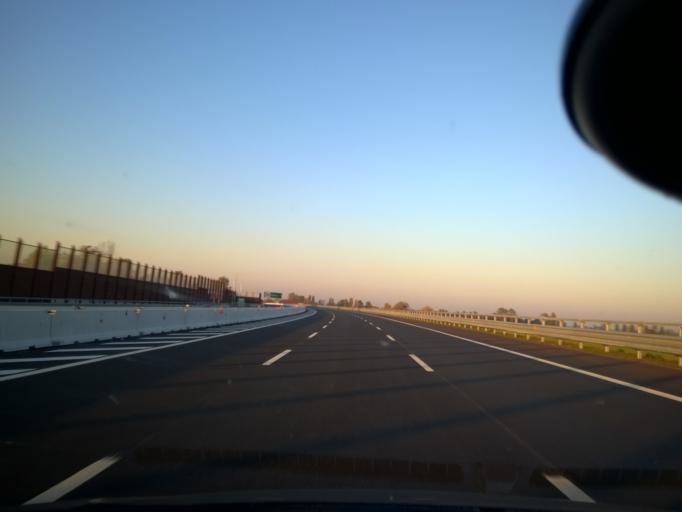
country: IT
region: Lombardy
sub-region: Citta metropolitana di Milano
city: Dresano
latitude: 45.3757
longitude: 9.3749
